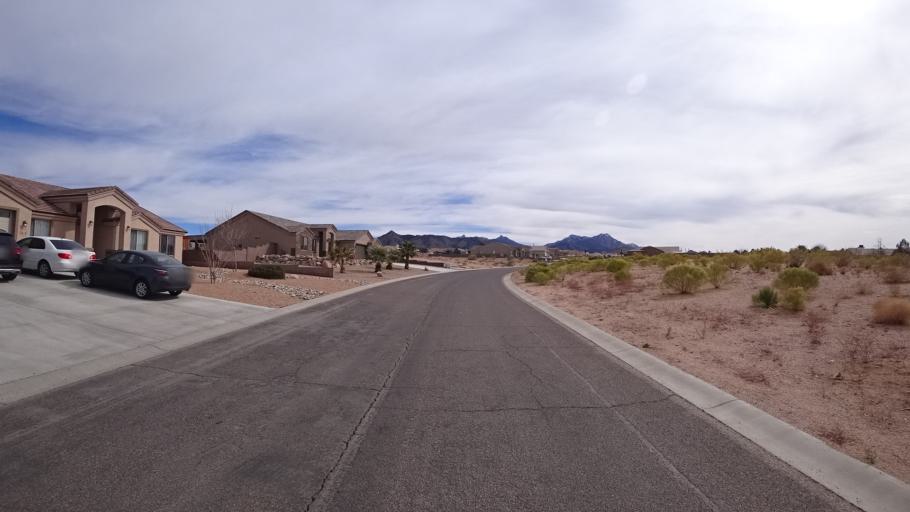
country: US
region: Arizona
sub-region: Mohave County
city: Kingman
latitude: 35.1931
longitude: -113.9827
